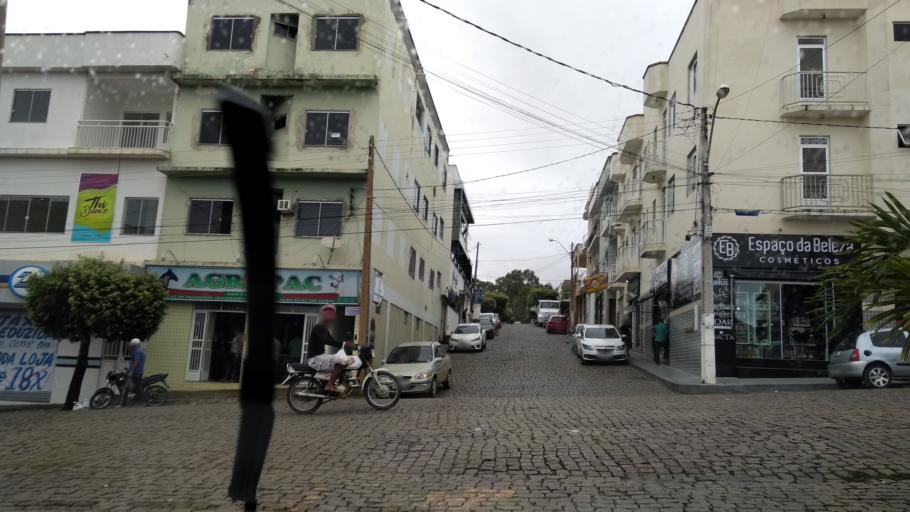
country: BR
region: Bahia
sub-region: Caetite
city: Caetite
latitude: -14.0662
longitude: -42.4919
